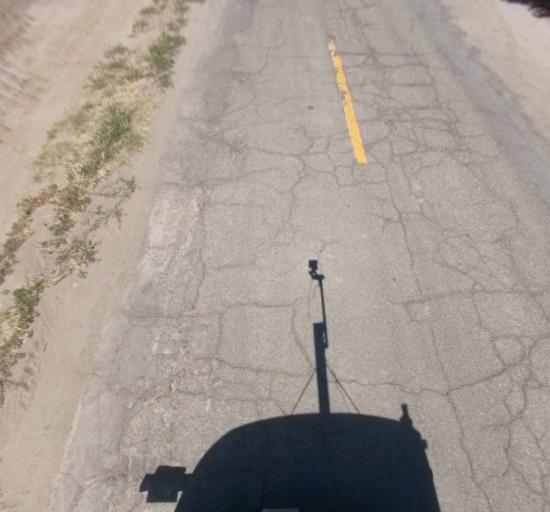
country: US
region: California
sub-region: Madera County
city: Chowchilla
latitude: 37.0399
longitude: -120.3411
